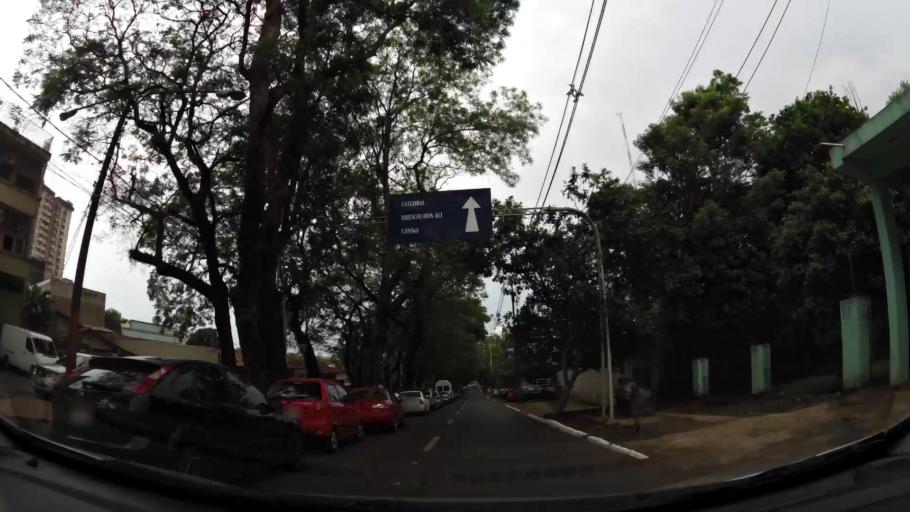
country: PY
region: Alto Parana
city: Ciudad del Este
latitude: -25.5194
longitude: -54.6111
